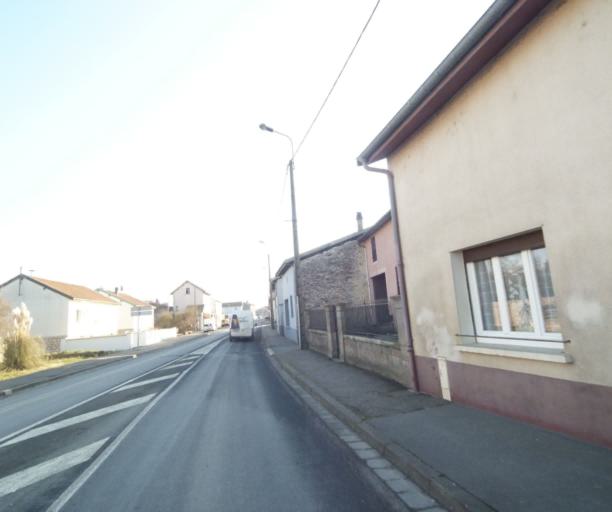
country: FR
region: Champagne-Ardenne
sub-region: Departement de la Haute-Marne
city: Chevillon
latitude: 48.5254
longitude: 5.1023
